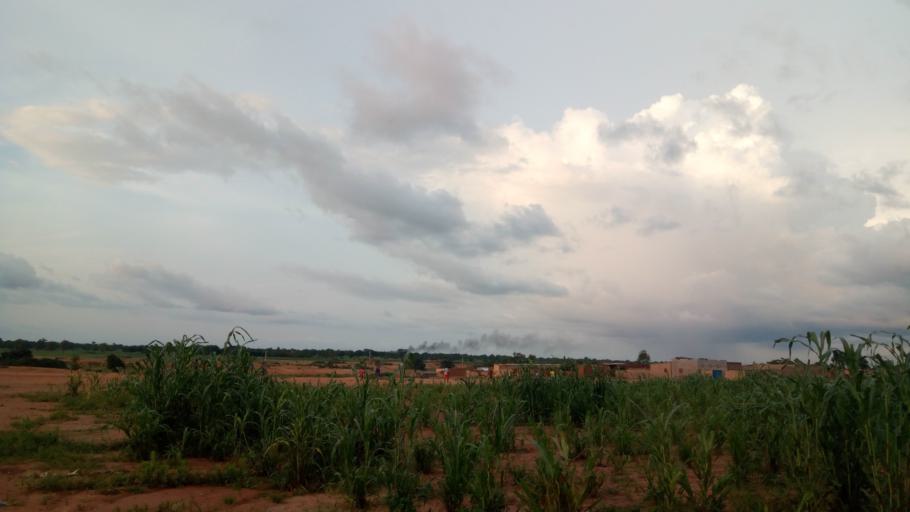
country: ML
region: Sikasso
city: Koutiala
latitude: 12.3788
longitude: -5.4975
